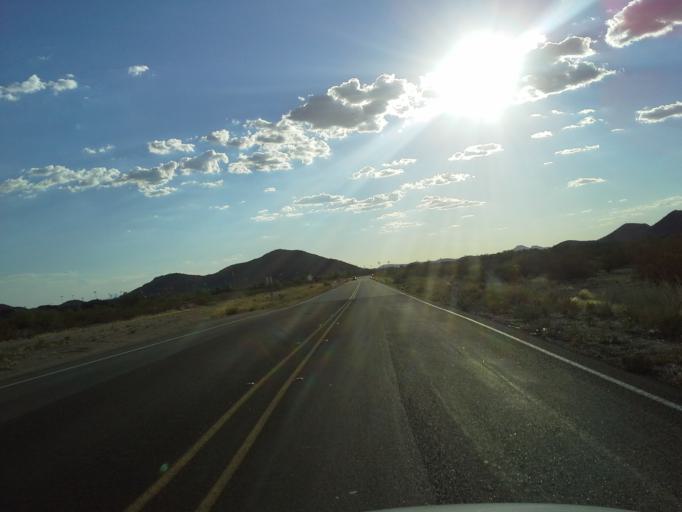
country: US
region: Arizona
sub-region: Maricopa County
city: Cave Creek
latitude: 33.6841
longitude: -112.0085
